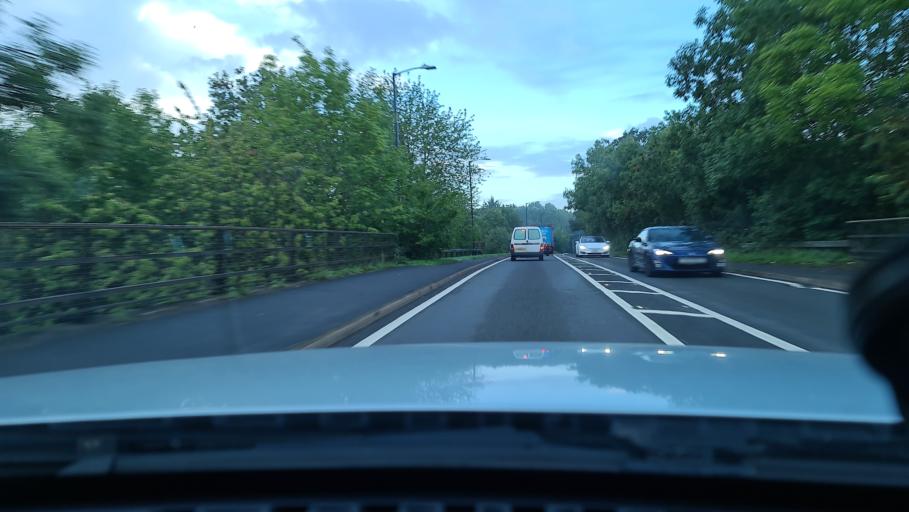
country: GB
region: England
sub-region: Warwickshire
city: Long Itchington
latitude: 52.2788
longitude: -1.3907
